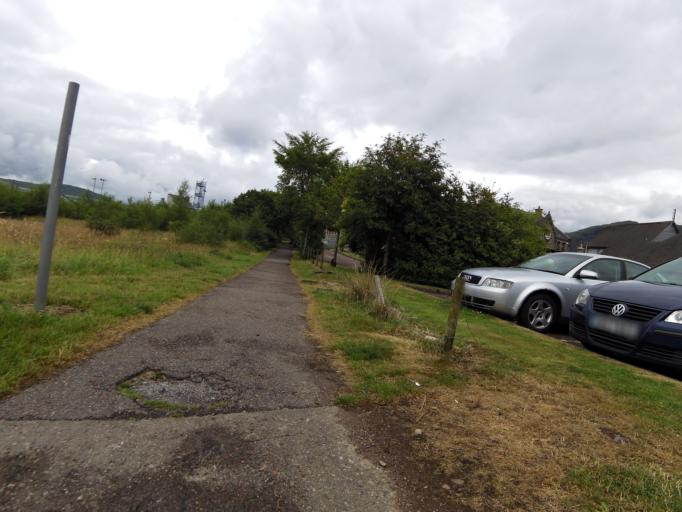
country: GB
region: Scotland
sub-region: Highland
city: Fort William
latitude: 56.8225
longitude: -5.1056
